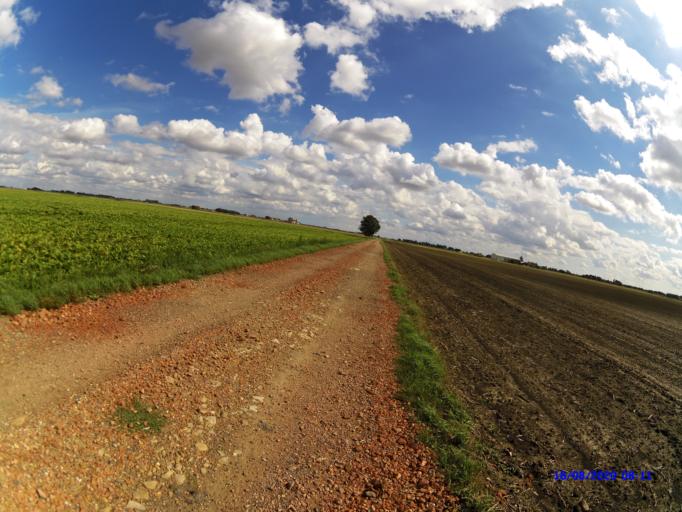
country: GB
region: England
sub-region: Cambridgeshire
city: Ramsey
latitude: 52.5102
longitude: -0.0805
